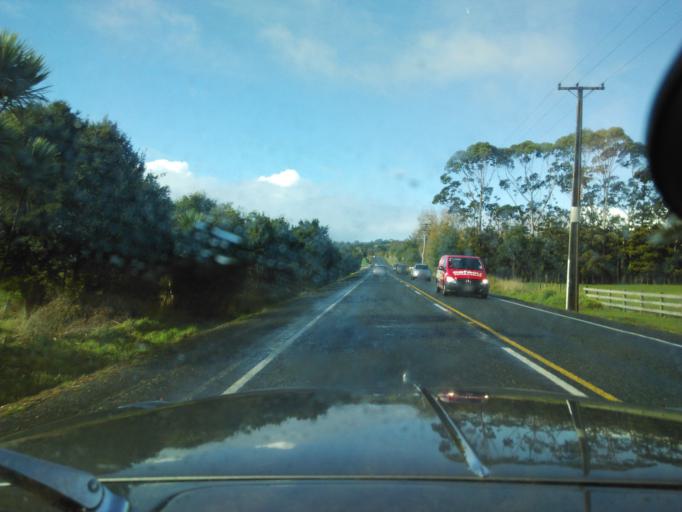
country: NZ
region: Auckland
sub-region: Auckland
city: Parakai
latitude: -36.6414
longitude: 174.5770
